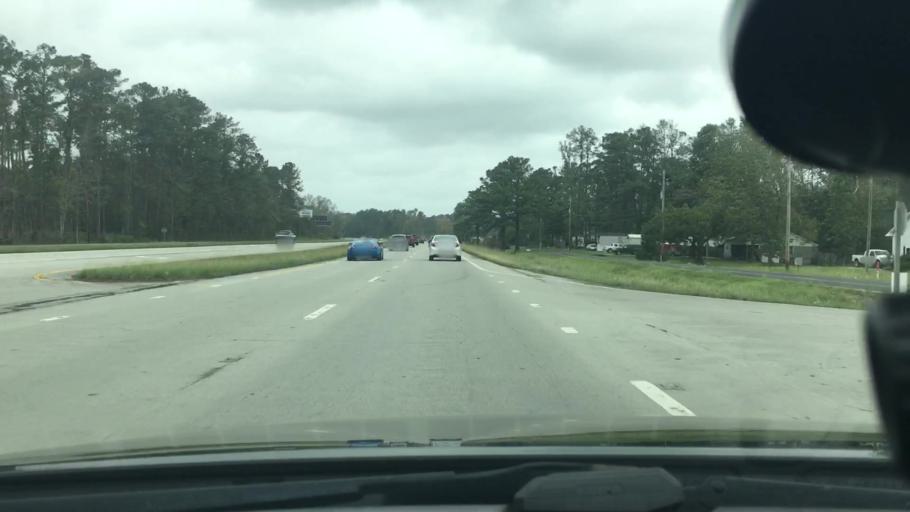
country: US
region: North Carolina
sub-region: Craven County
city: Neuse Forest
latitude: 34.9475
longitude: -76.9483
